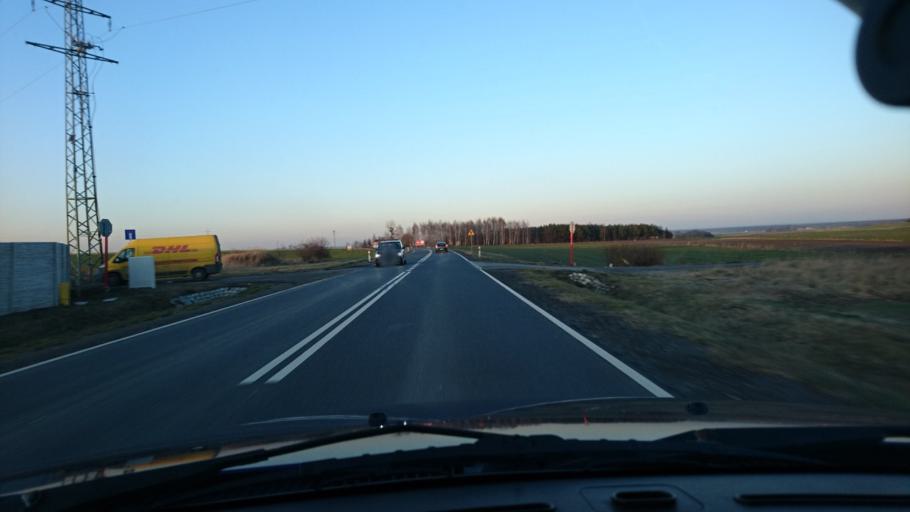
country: PL
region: Silesian Voivodeship
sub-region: Powiat gliwicki
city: Wielowies
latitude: 50.4910
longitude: 18.6068
